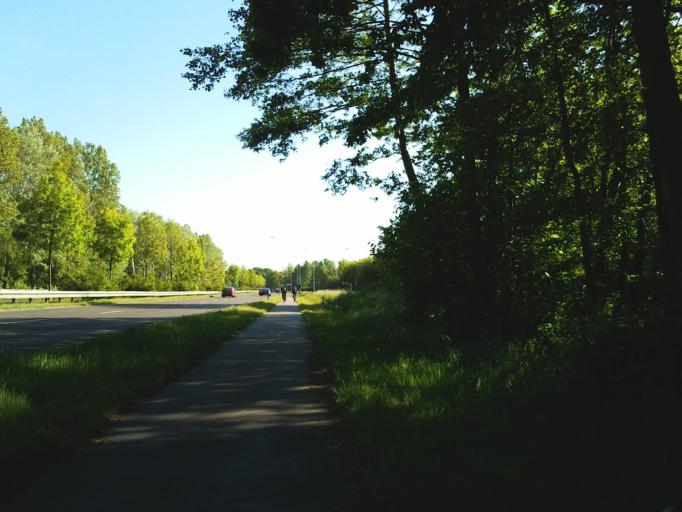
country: DE
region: Mecklenburg-Vorpommern
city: Warnemuende
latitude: 54.1462
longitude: 12.0662
